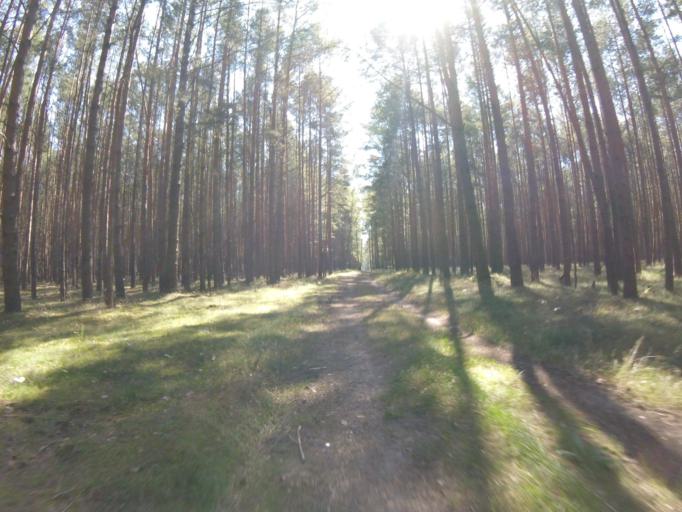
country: DE
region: Brandenburg
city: Bestensee
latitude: 52.2637
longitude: 13.6765
